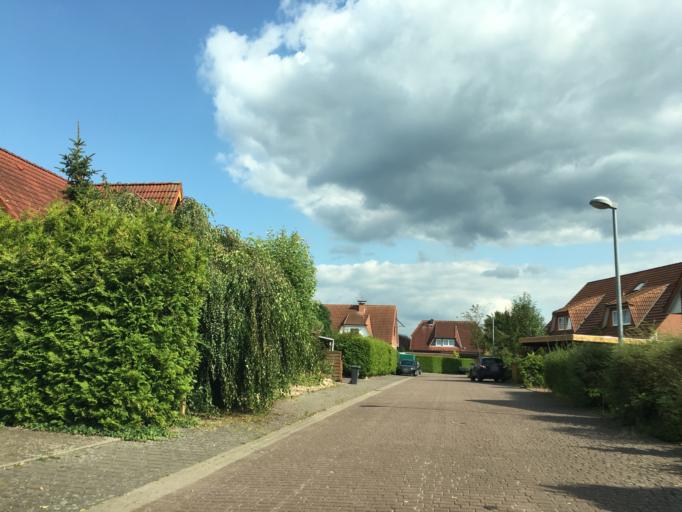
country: DE
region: Lower Saxony
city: Melbeck
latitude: 53.2082
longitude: 10.3896
